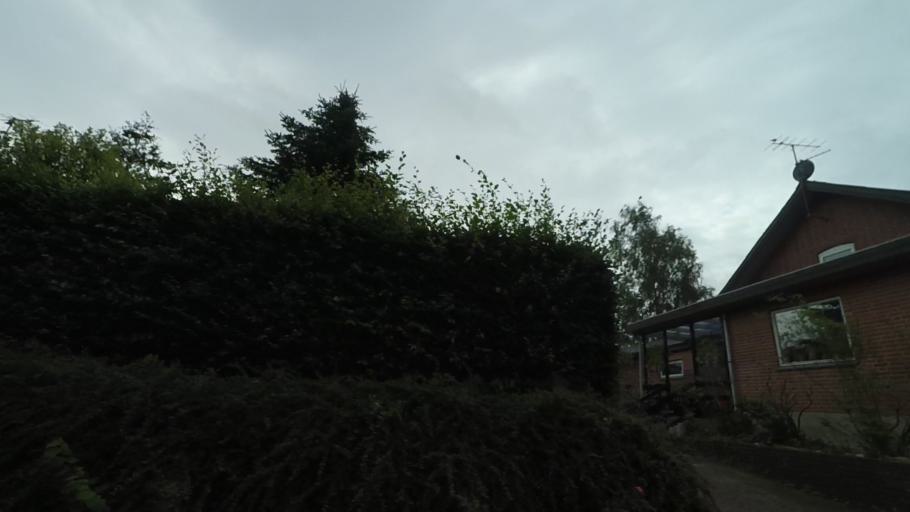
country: DK
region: Central Jutland
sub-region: Syddjurs Kommune
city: Ronde
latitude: 56.3414
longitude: 10.4616
